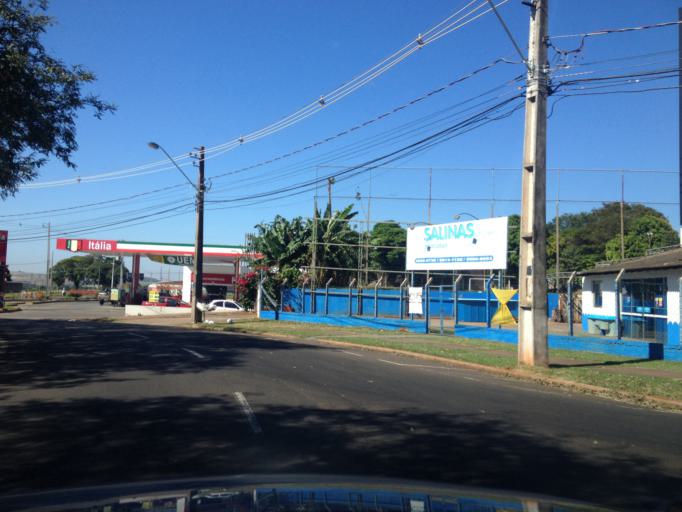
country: BR
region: Parana
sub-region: Maringa
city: Maringa
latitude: -23.4483
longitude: -51.9446
